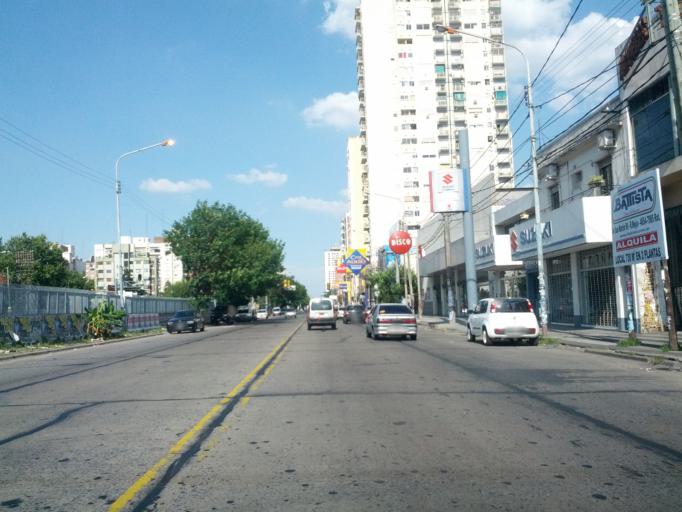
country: AR
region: Buenos Aires
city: San Justo
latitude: -34.6418
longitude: -58.5716
